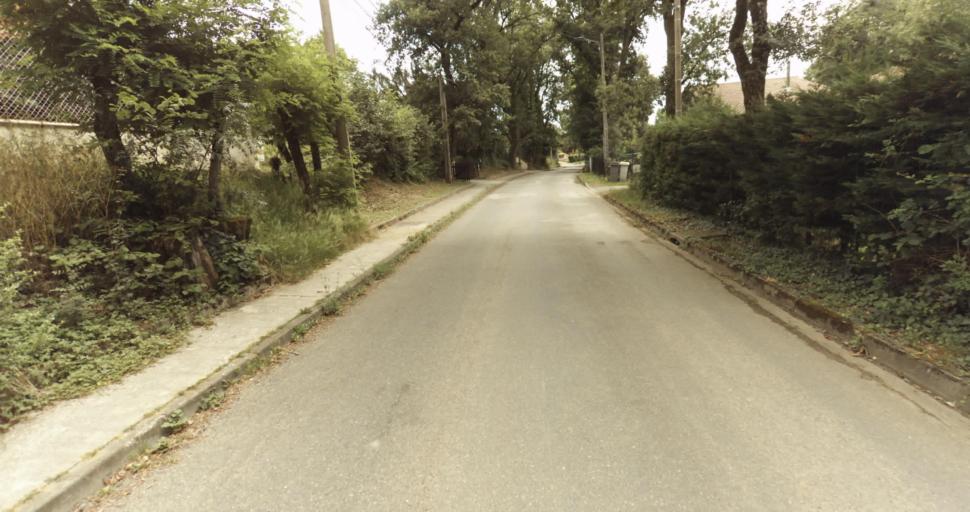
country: FR
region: Midi-Pyrenees
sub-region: Departement de la Haute-Garonne
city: Fontenilles
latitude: 43.5550
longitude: 1.1896
